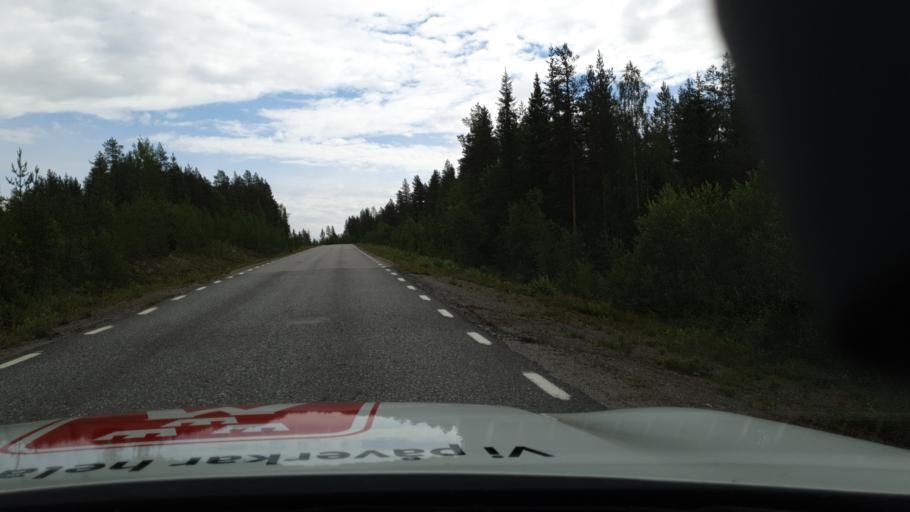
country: SE
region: Vaesterbotten
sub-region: Sorsele Kommun
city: Sorsele
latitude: 65.5444
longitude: 17.4528
